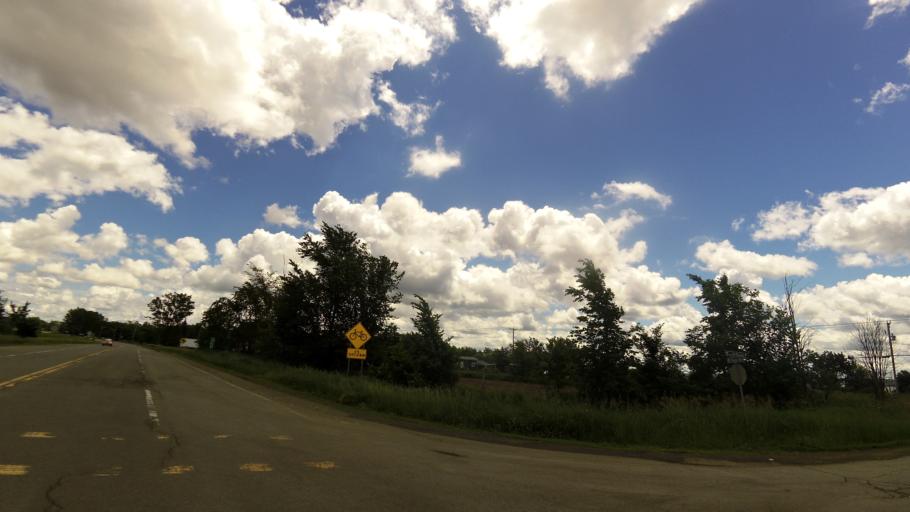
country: CA
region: Quebec
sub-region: Monteregie
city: Hudson
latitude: 45.5289
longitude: -74.1990
